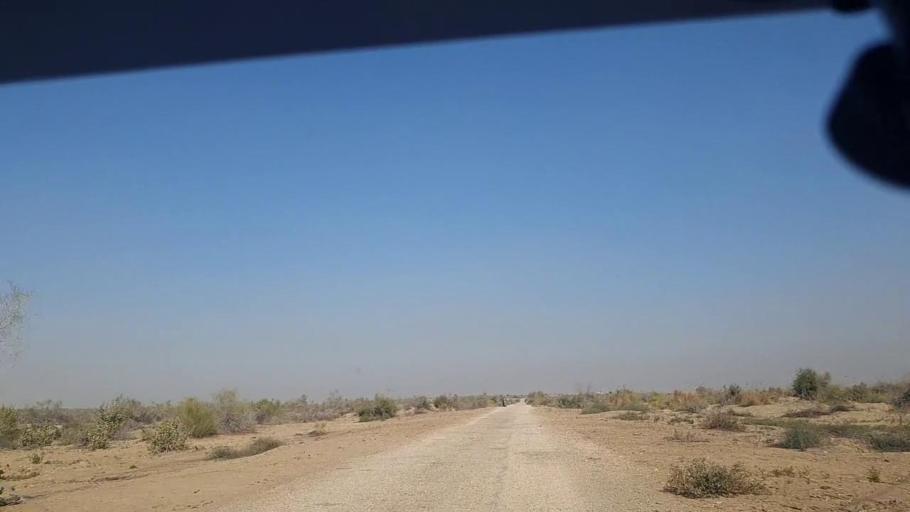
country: PK
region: Sindh
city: Khanpur
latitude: 27.5694
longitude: 69.3432
